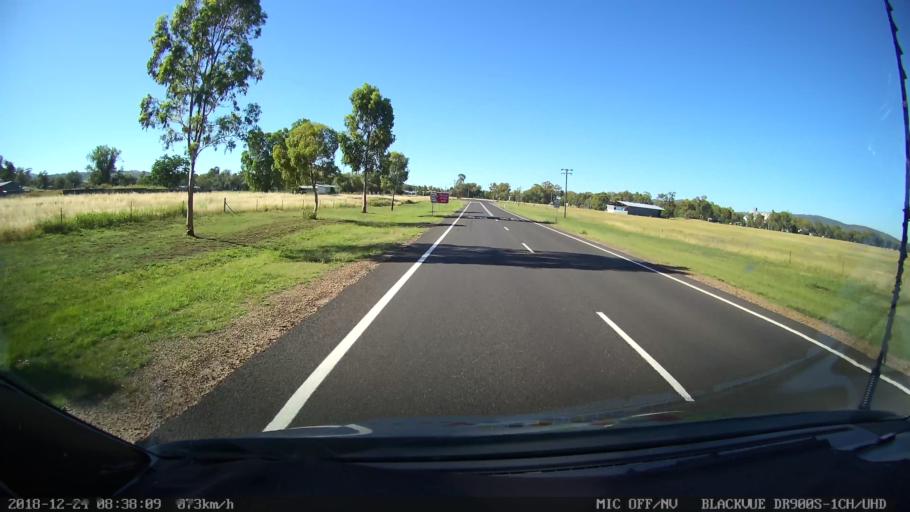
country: AU
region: New South Wales
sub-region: Liverpool Plains
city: Quirindi
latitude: -31.3383
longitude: 150.6476
